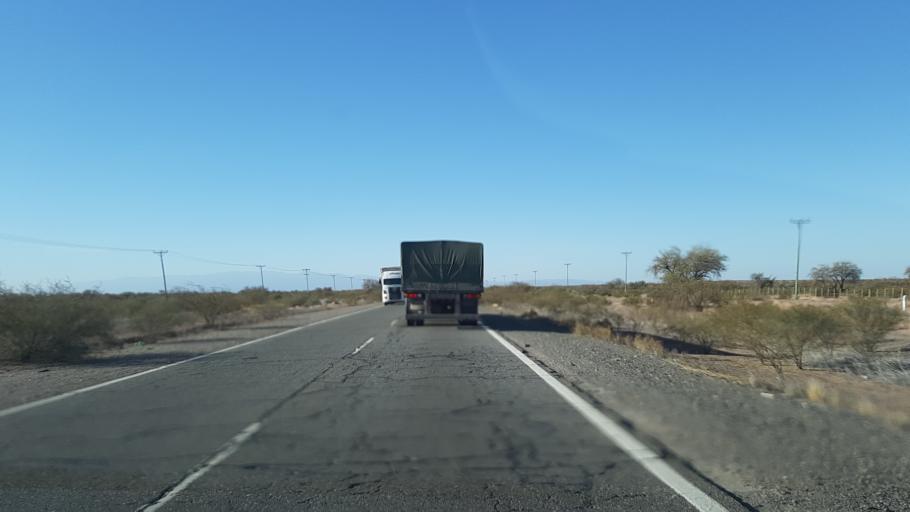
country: AR
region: San Juan
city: Caucete
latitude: -31.6499
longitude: -67.7643
